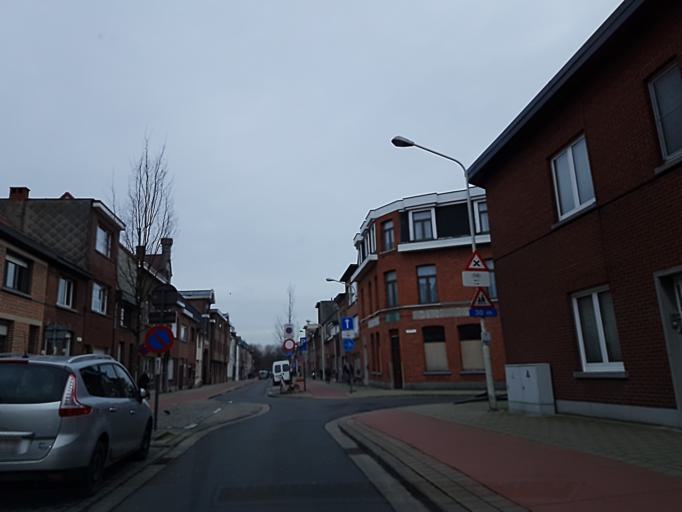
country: BE
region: Flanders
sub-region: Provincie Antwerpen
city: Antwerpen
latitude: 51.2459
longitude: 4.4426
